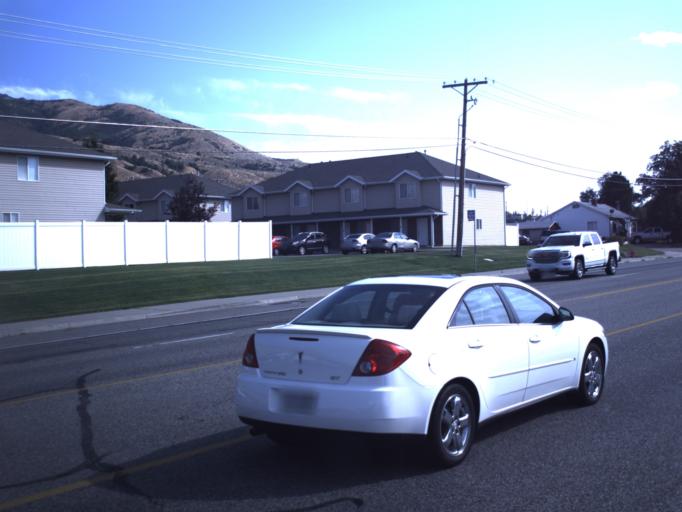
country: US
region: Utah
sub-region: Box Elder County
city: Perry
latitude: 41.4722
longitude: -112.0277
